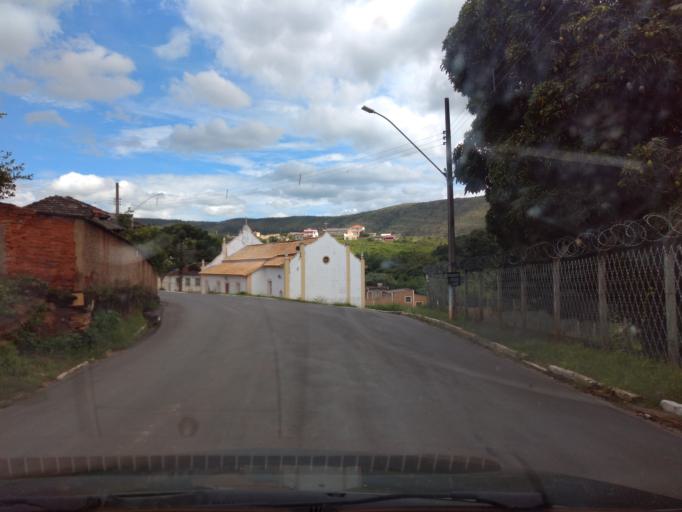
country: BR
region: Minas Gerais
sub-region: Lavras
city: Lavras
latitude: -21.5123
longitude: -44.9073
